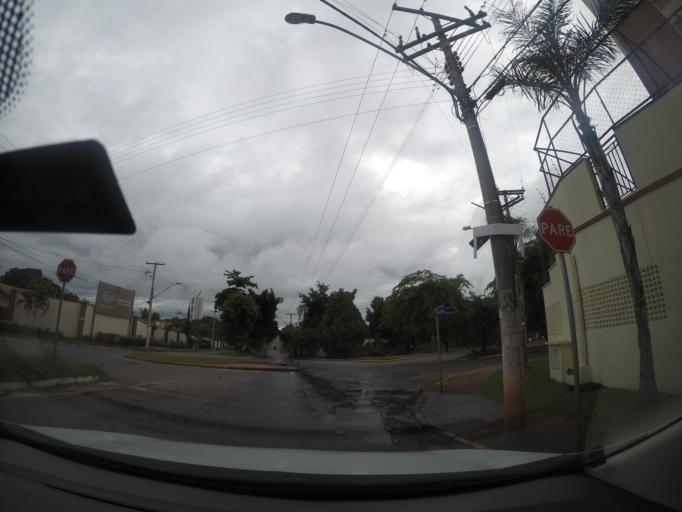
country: BR
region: Goias
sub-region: Goiania
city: Goiania
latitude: -16.7315
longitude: -49.2841
